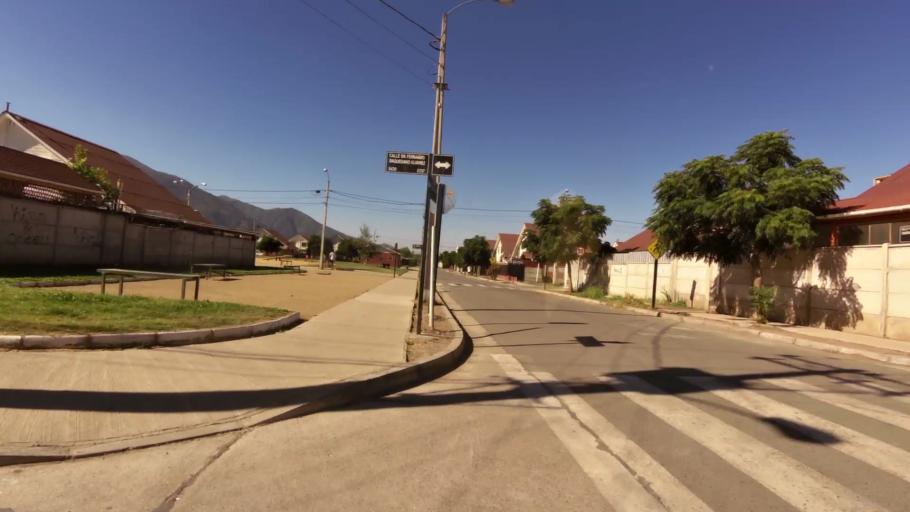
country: CL
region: O'Higgins
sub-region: Provincia de Colchagua
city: Chimbarongo
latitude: -34.5815
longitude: -71.0082
